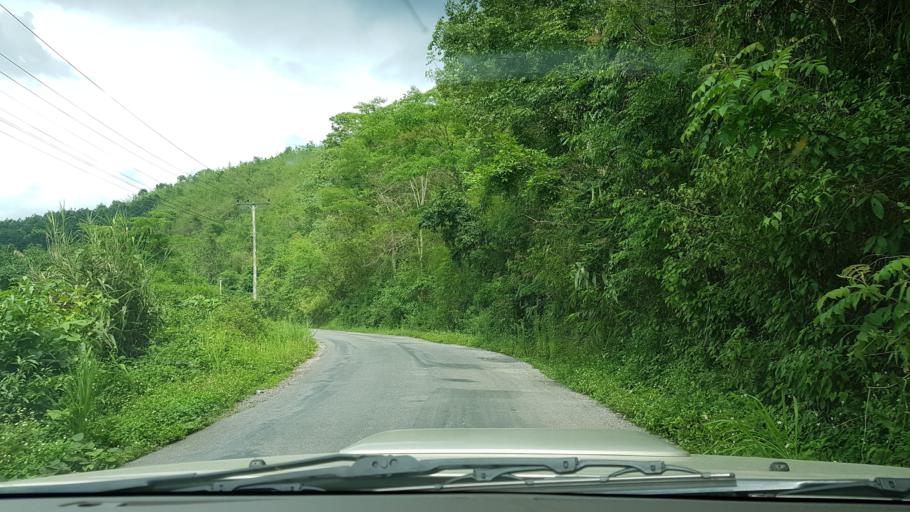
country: LA
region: Loungnamtha
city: Muang Nale
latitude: 20.3704
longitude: 101.7216
